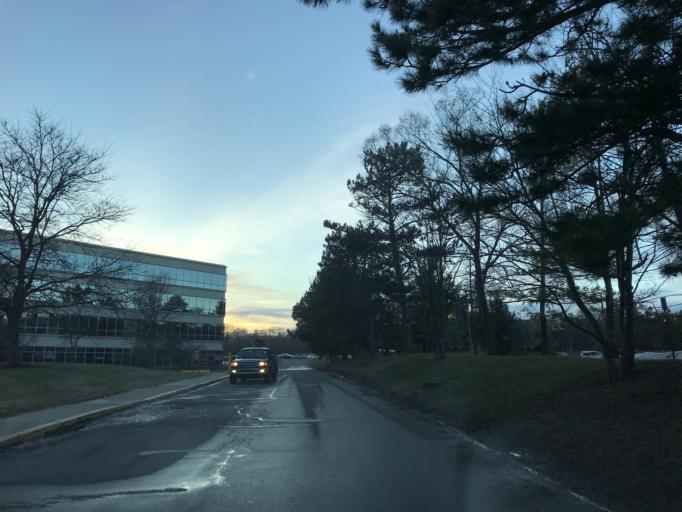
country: US
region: Michigan
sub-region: Oakland County
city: Bingham Farms
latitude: 42.5146
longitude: -83.2832
